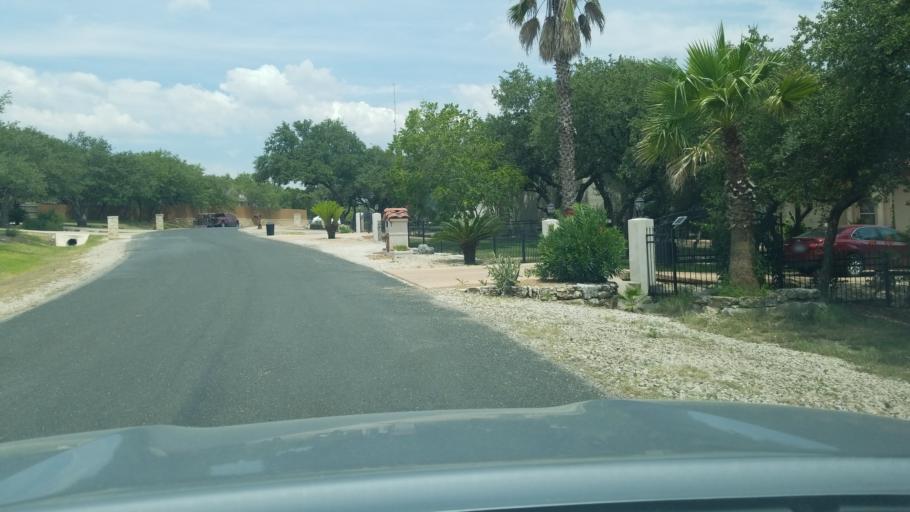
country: US
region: Texas
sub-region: Bexar County
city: Timberwood Park
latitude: 29.6907
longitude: -98.5070
